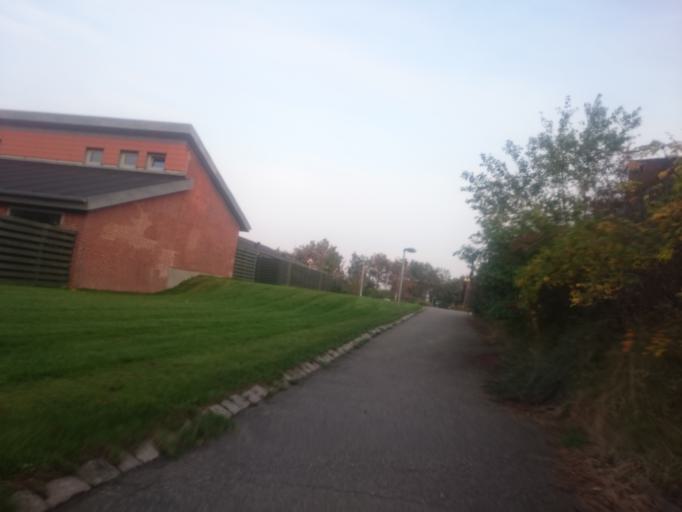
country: DK
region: South Denmark
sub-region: Billund Kommune
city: Billund
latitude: 55.7279
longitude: 9.1043
